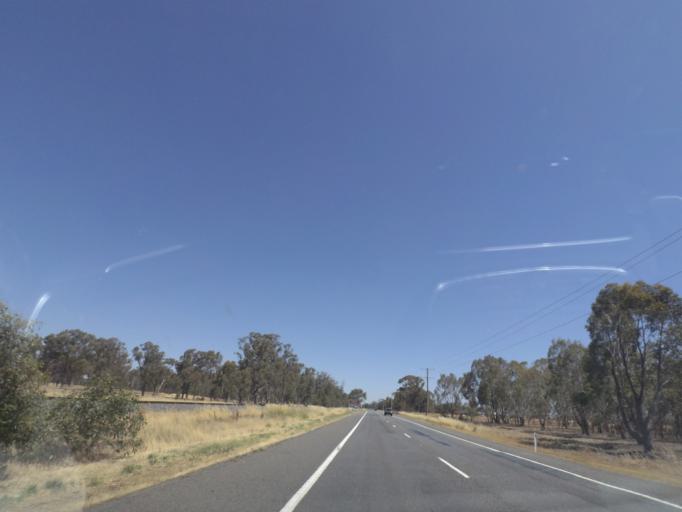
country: AU
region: Victoria
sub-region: Greater Shepparton
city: Shepparton
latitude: -36.2259
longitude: 145.4318
